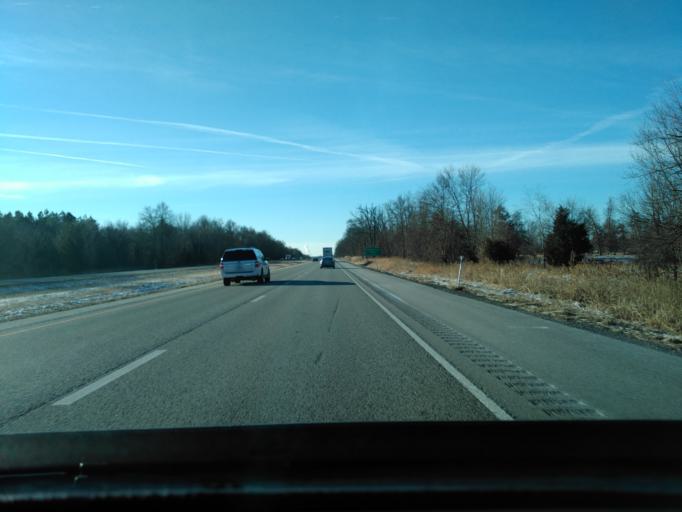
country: US
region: Illinois
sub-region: Williamson County
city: Johnston City
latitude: 37.8359
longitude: -88.9449
